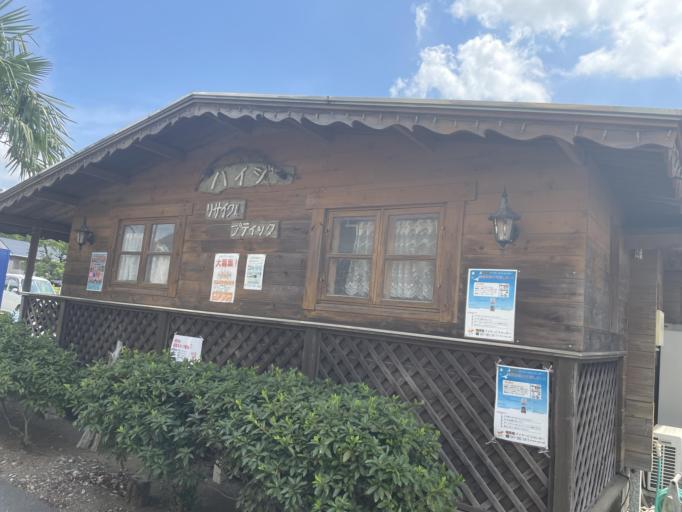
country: JP
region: Chiba
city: Kashiwa
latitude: 35.8023
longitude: 139.9653
